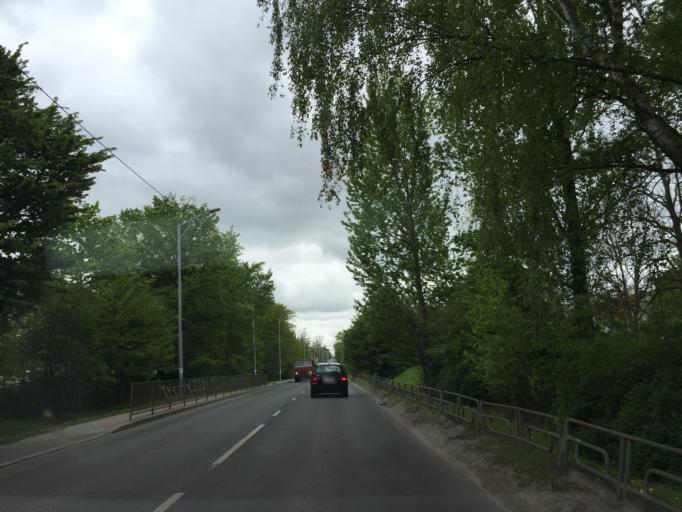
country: RU
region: Kaliningrad
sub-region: Gorod Kaliningrad
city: Kaliningrad
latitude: 54.6767
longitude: 20.4431
